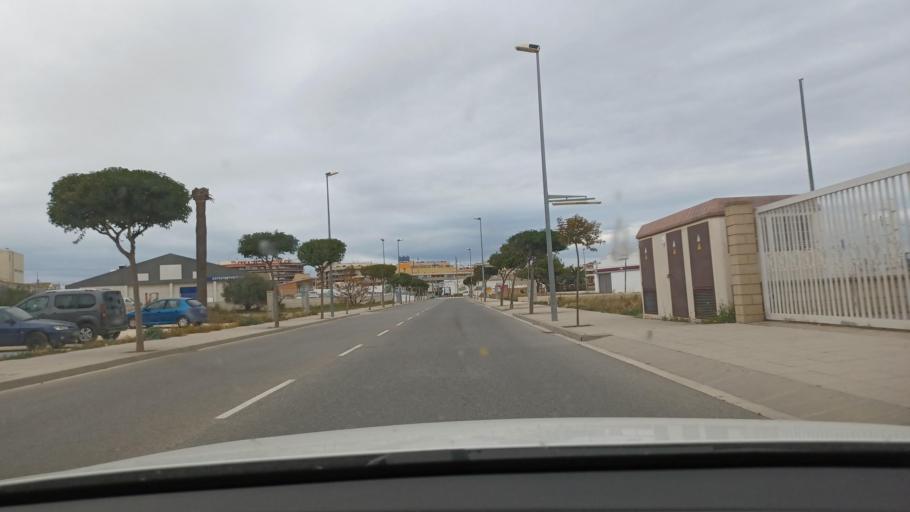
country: ES
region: Catalonia
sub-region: Provincia de Tarragona
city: Amposta
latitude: 40.6990
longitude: 0.5796
